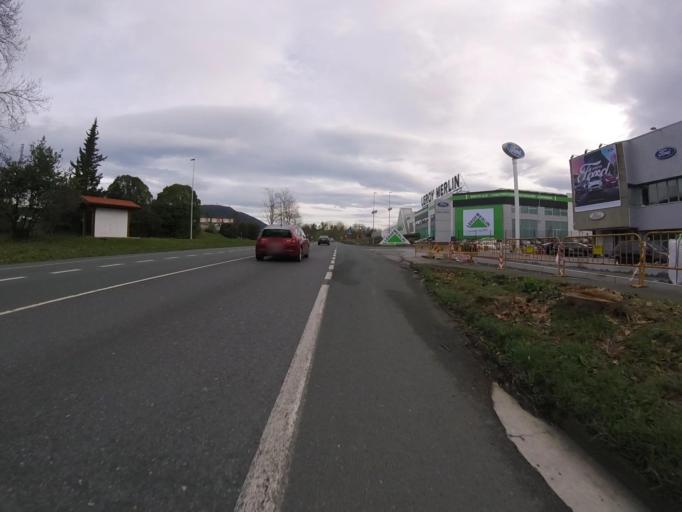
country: ES
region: Basque Country
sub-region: Provincia de Guipuzcoa
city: Lezo
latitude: 43.3134
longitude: -1.8771
